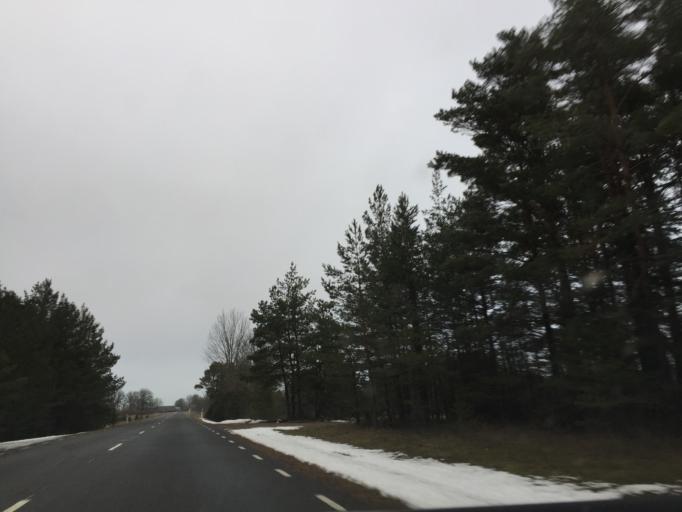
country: EE
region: Saare
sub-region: Kuressaare linn
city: Kuressaare
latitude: 58.5571
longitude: 22.3152
